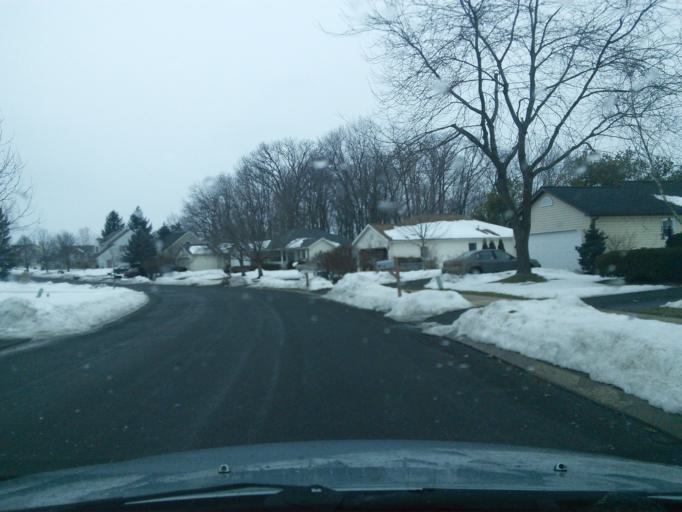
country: US
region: Pennsylvania
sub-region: Centre County
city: State College
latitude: 40.7691
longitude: -77.8734
